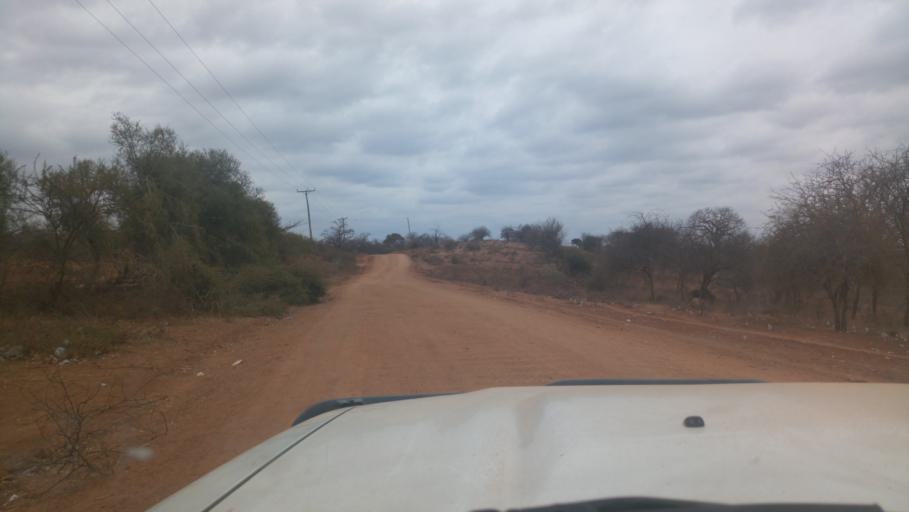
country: KE
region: Makueni
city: Makueni
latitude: -1.9698
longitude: 38.0956
